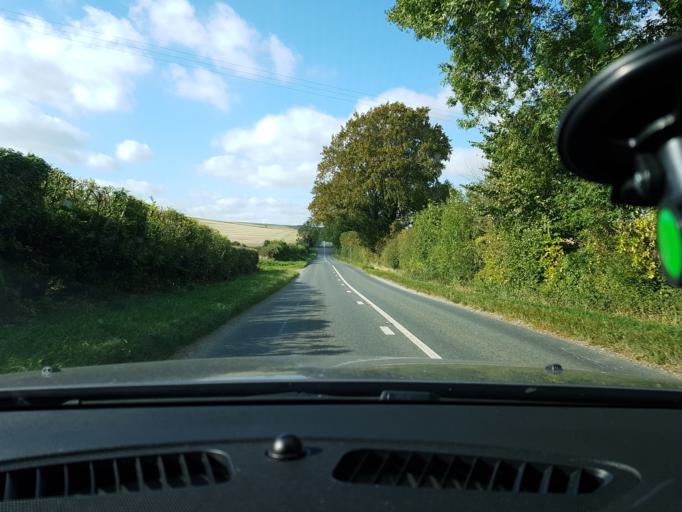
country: GB
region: England
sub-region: Wiltshire
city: Aldbourne
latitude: 51.4975
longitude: -1.6557
